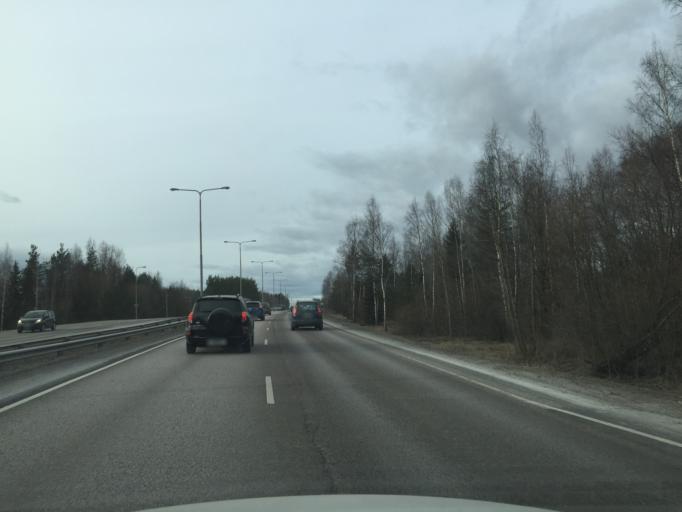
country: FI
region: Uusimaa
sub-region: Helsinki
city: Teekkarikylae
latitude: 60.2751
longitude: 24.8710
